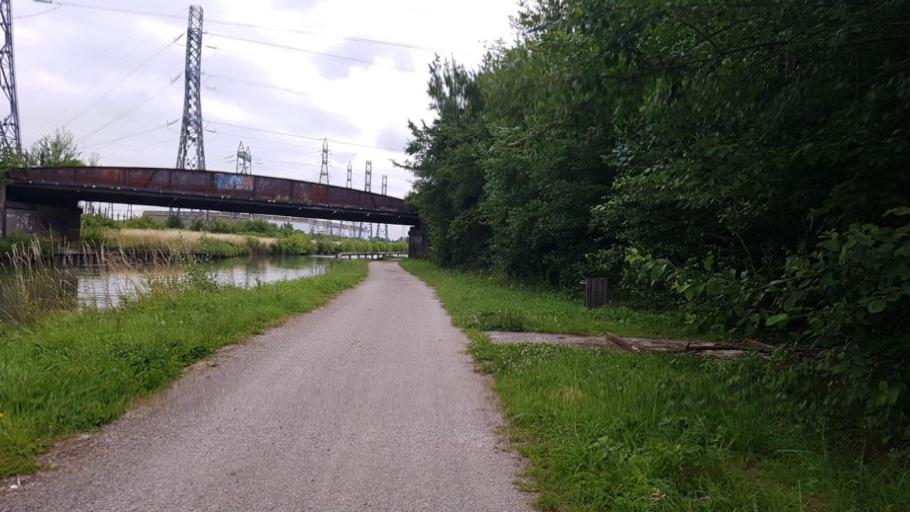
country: FR
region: Picardie
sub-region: Departement de l'Aisne
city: Beautor
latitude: 49.6521
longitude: 3.3242
